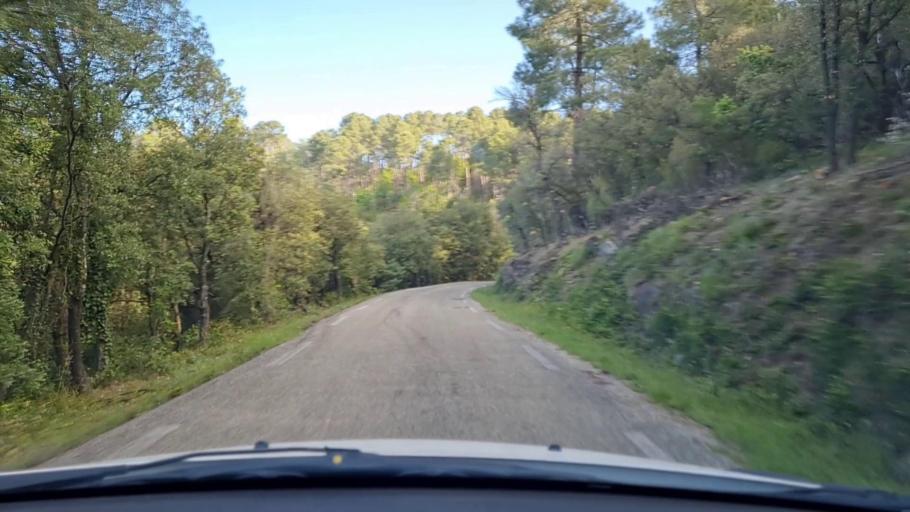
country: FR
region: Languedoc-Roussillon
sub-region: Departement du Gard
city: Branoux-les-Taillades
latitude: 44.1830
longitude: 4.0066
